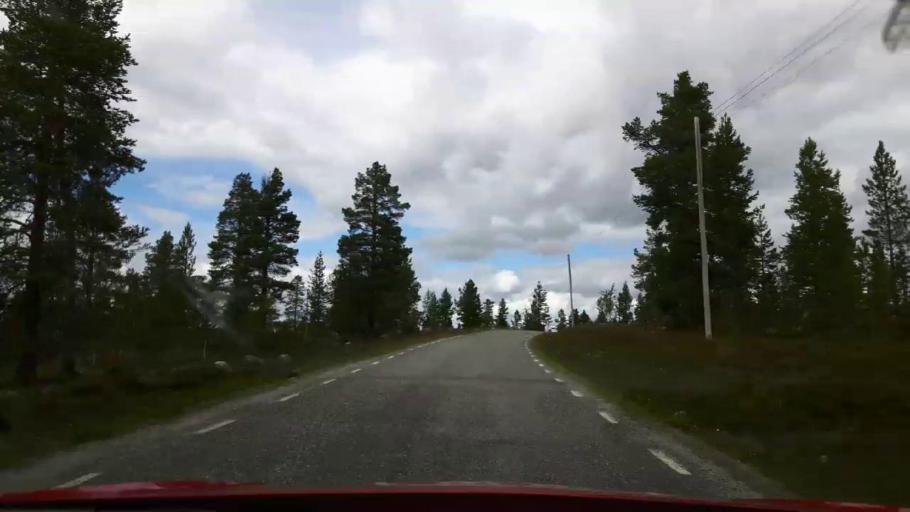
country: NO
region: Hedmark
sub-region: Engerdal
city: Engerdal
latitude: 62.3152
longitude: 12.8088
